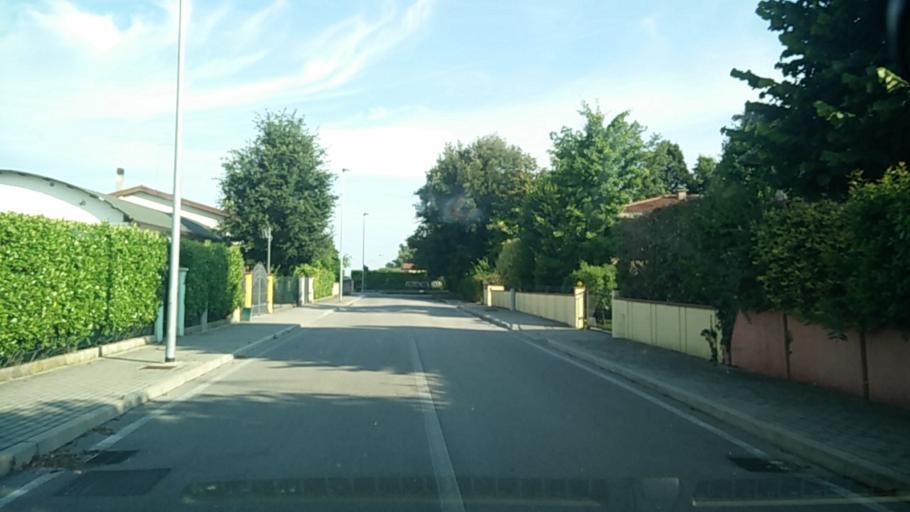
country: IT
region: Veneto
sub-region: Provincia di Venezia
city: Musile di Piave
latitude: 45.6192
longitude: 12.5317
